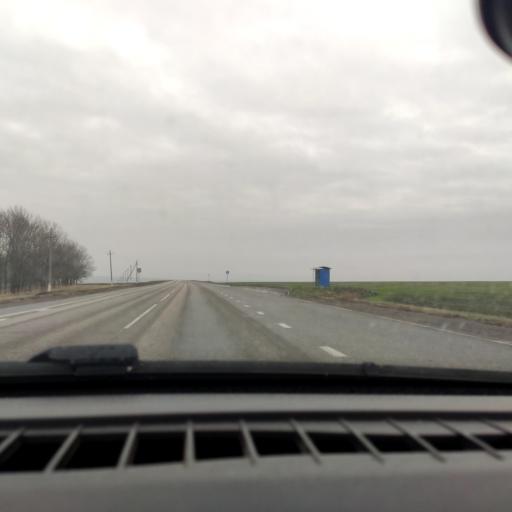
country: RU
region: Belgorod
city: Ilovka
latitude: 50.7725
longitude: 38.7775
